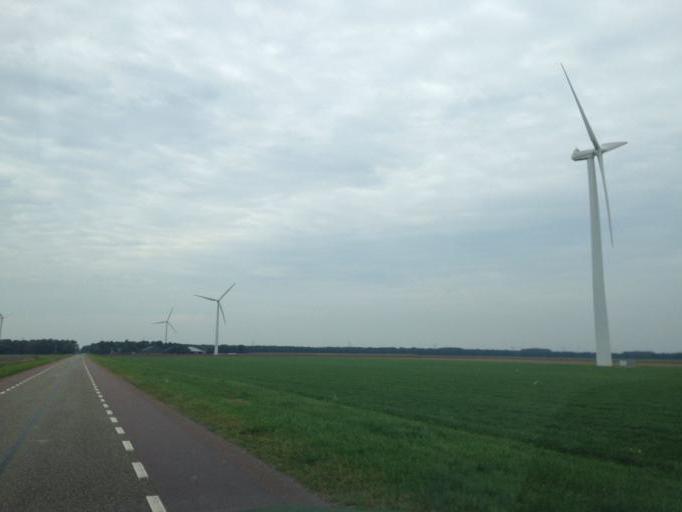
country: NL
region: Flevoland
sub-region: Gemeente Lelystad
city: Lelystad
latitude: 52.4083
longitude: 5.4177
